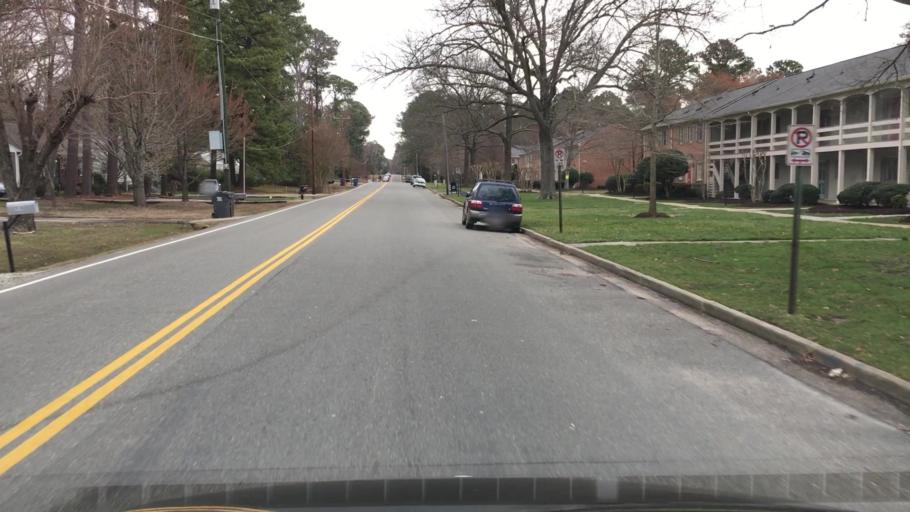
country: US
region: Virginia
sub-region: Henrico County
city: Tuckahoe
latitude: 37.5883
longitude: -77.5854
